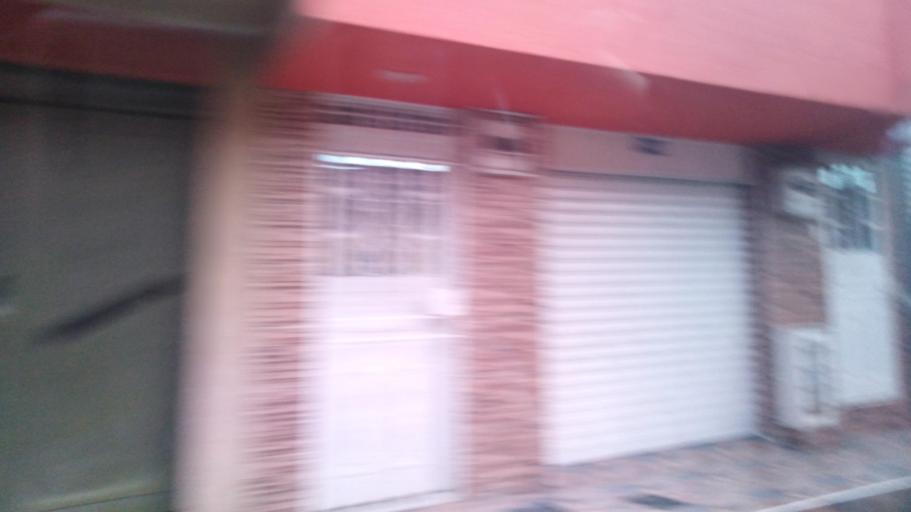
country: CO
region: Valle del Cauca
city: Cali
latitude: 3.4436
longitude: -76.5333
